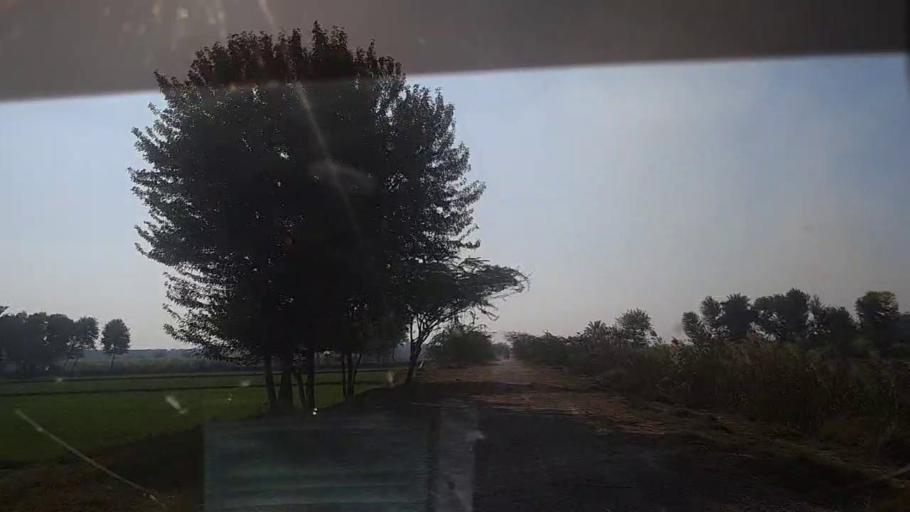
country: PK
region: Sindh
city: Gambat
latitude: 27.3745
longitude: 68.5728
